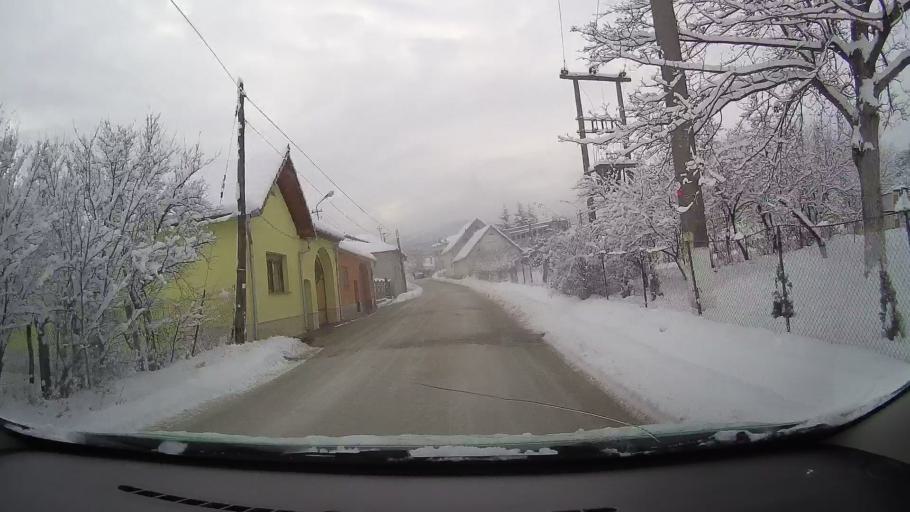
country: RO
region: Alba
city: Pianu de Sus
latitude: 45.9043
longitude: 23.4803
